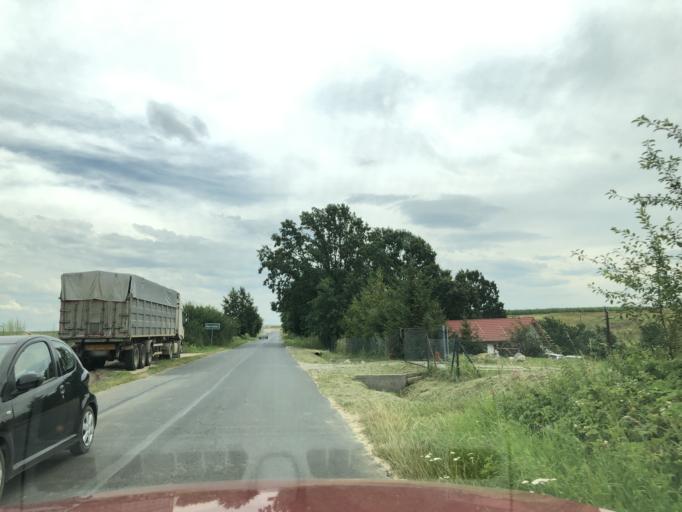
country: PL
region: Lower Silesian Voivodeship
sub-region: Powiat trzebnicki
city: Trzebnica
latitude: 51.3221
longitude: 17.0302
